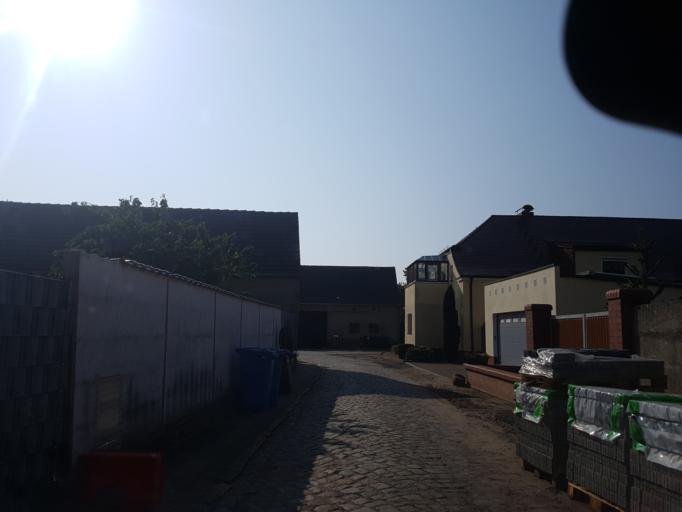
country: DE
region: Brandenburg
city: Wiesenburg
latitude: 52.0576
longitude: 12.3796
